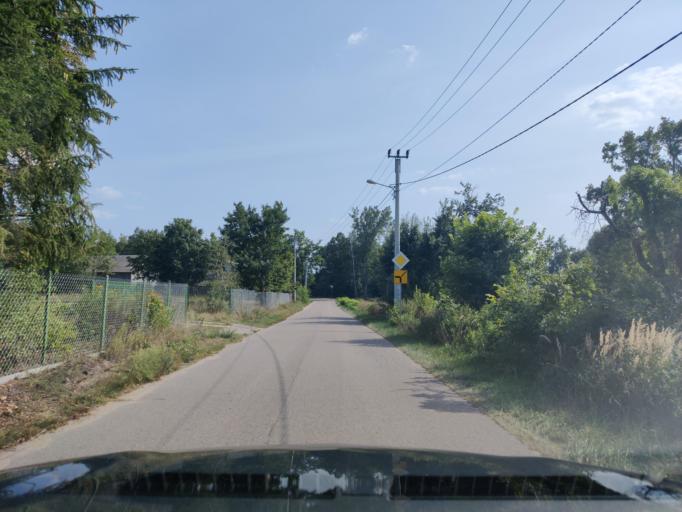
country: PL
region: Masovian Voivodeship
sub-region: Powiat makowski
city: Rozan
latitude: 52.8486
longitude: 21.4573
